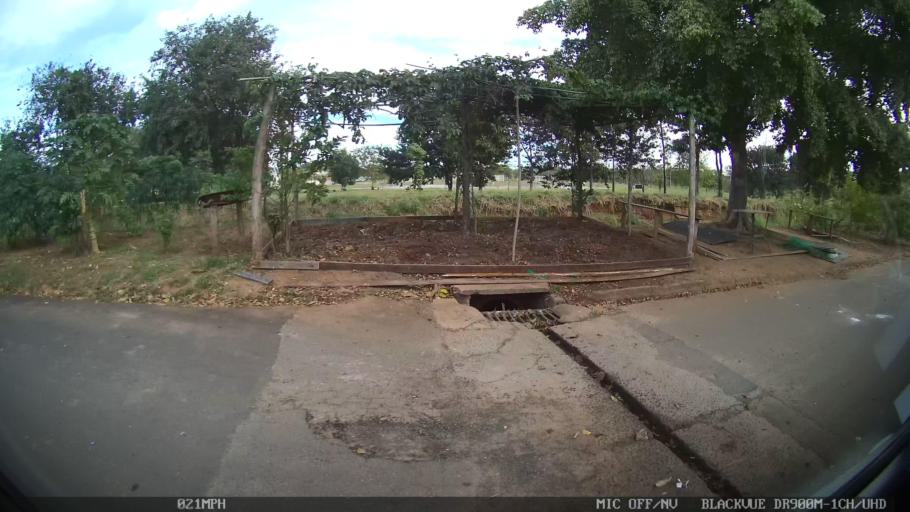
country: BR
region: Sao Paulo
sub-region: Catanduva
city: Catanduva
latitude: -21.1242
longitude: -48.9829
